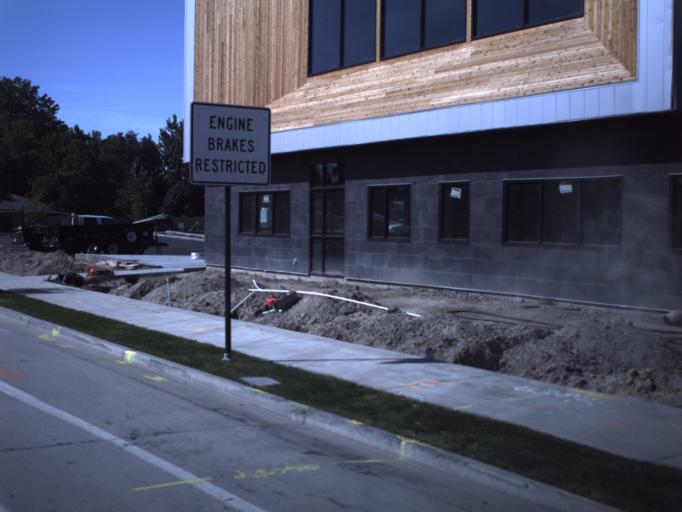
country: US
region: Utah
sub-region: Salt Lake County
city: South Jordan Heights
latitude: 40.5624
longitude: -111.9406
